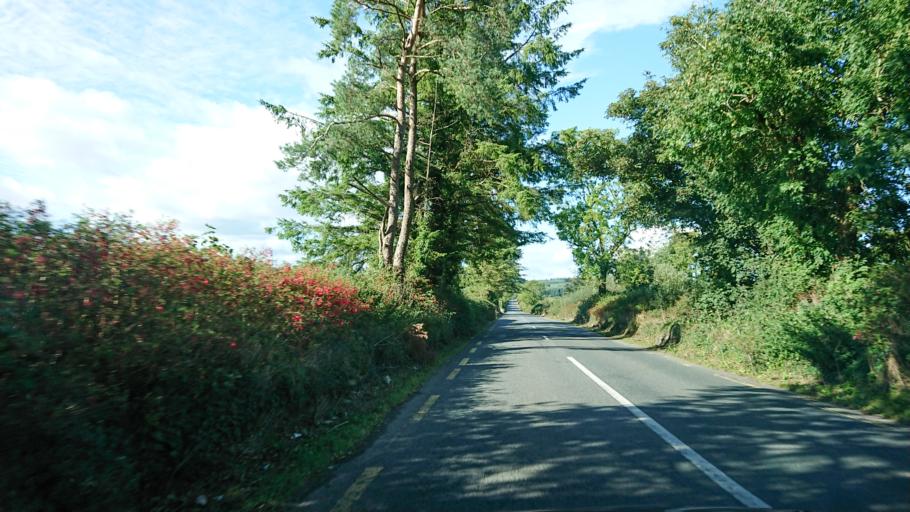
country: IE
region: Munster
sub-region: Waterford
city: Dungarvan
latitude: 52.1967
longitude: -7.6995
